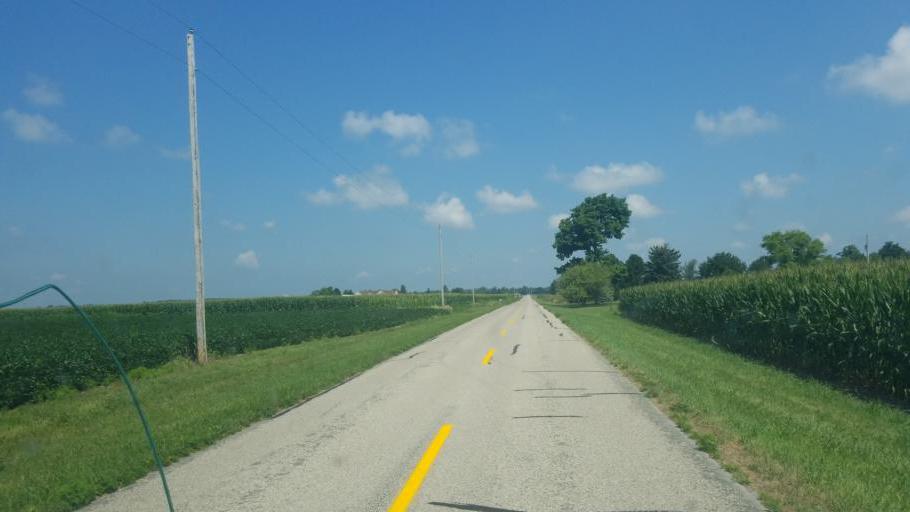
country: US
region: Ohio
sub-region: Hardin County
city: Ada
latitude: 40.6877
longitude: -83.9101
